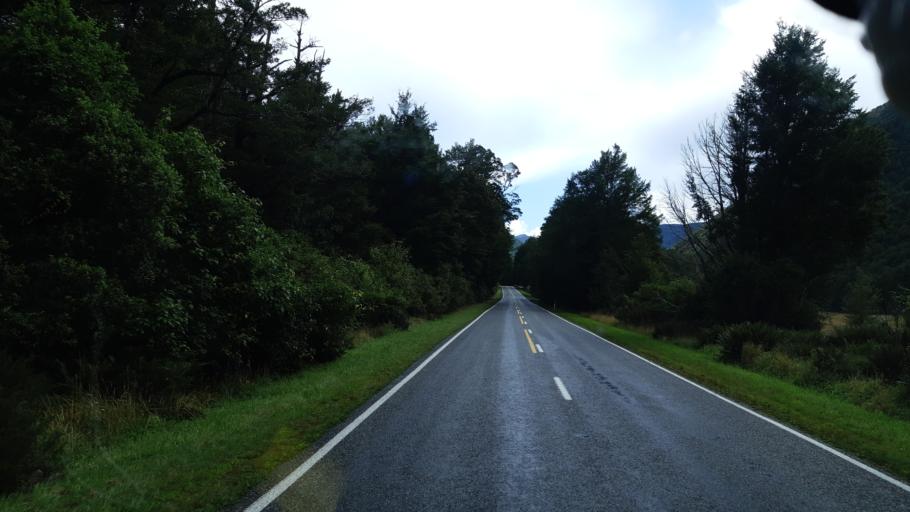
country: NZ
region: Canterbury
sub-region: Hurunui District
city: Amberley
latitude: -42.3806
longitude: 172.3176
